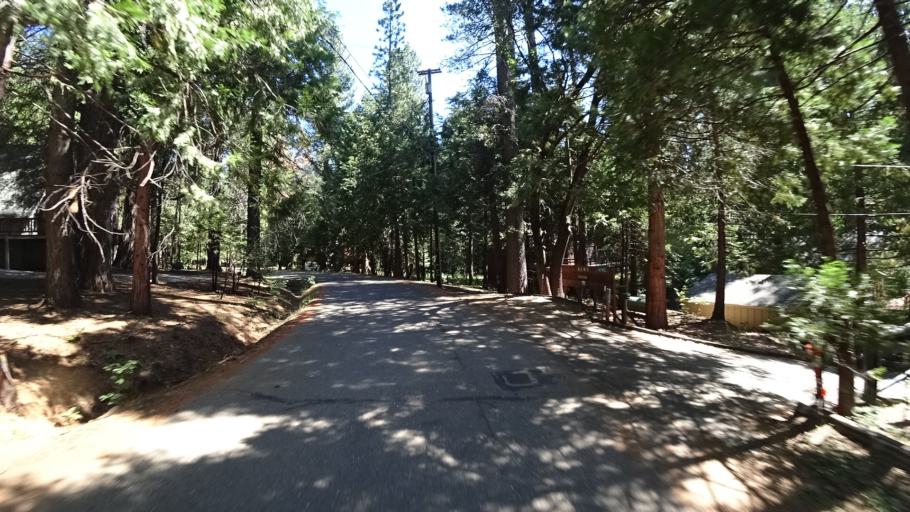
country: US
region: California
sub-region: Calaveras County
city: Arnold
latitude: 38.2357
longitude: -120.3768
